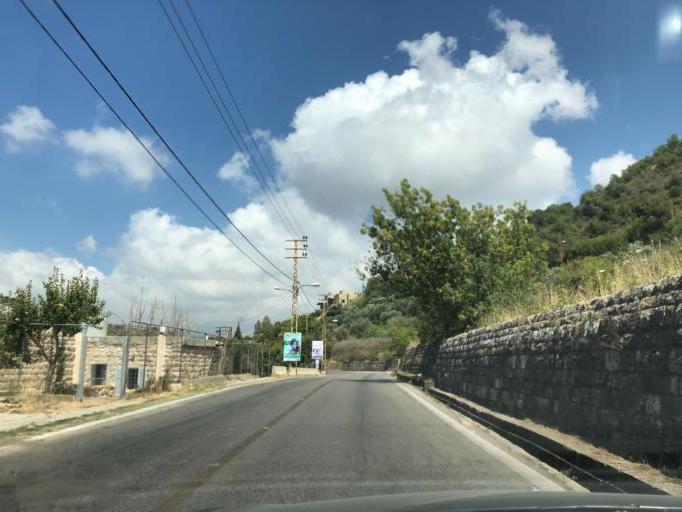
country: LB
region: Mont-Liban
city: Beit ed Dine
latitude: 33.6979
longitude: 35.5916
